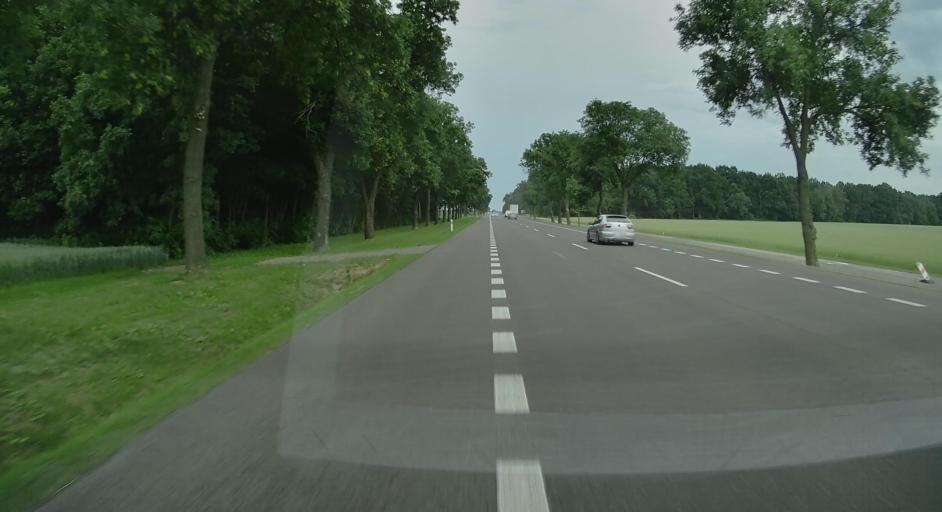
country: PL
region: Lublin Voivodeship
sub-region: Powiat bialski
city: Rzeczyca
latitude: 52.0135
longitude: 22.7354
